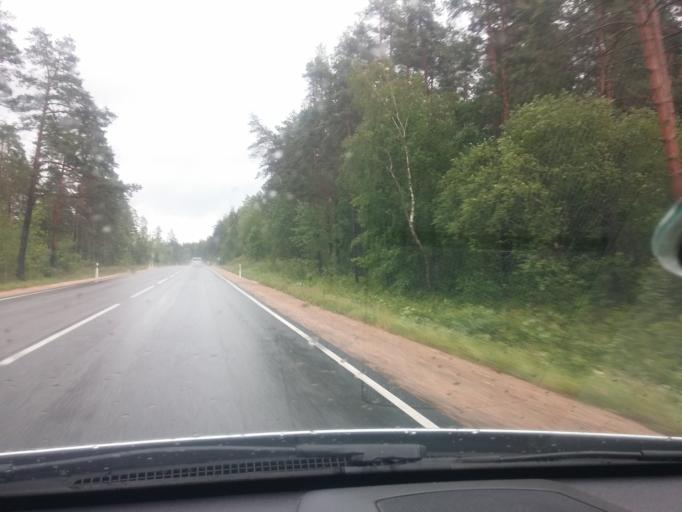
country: LV
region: Ikskile
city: Ikskile
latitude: 56.8944
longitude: 24.4435
